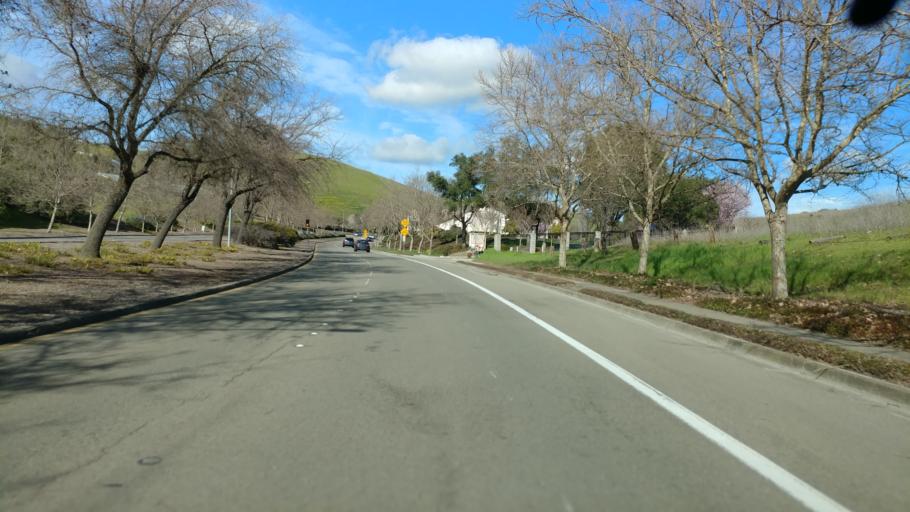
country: US
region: California
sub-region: Contra Costa County
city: San Ramon
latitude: 37.7847
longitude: -121.9356
